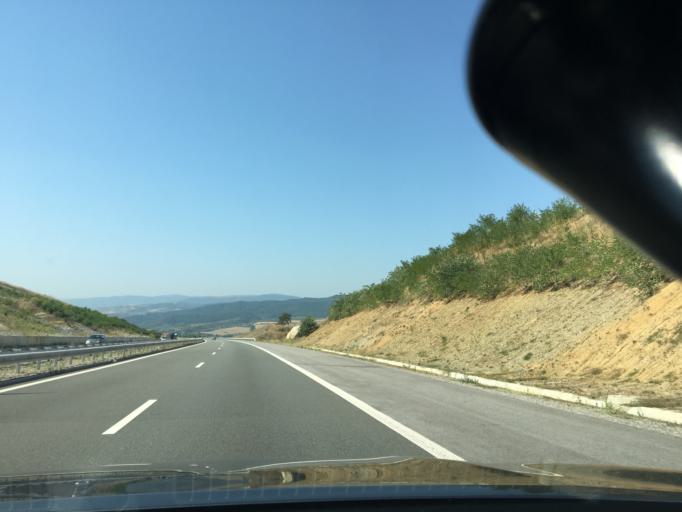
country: BG
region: Kyustendil
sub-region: Obshtina Dupnitsa
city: Dupnitsa
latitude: 42.2836
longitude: 23.0833
